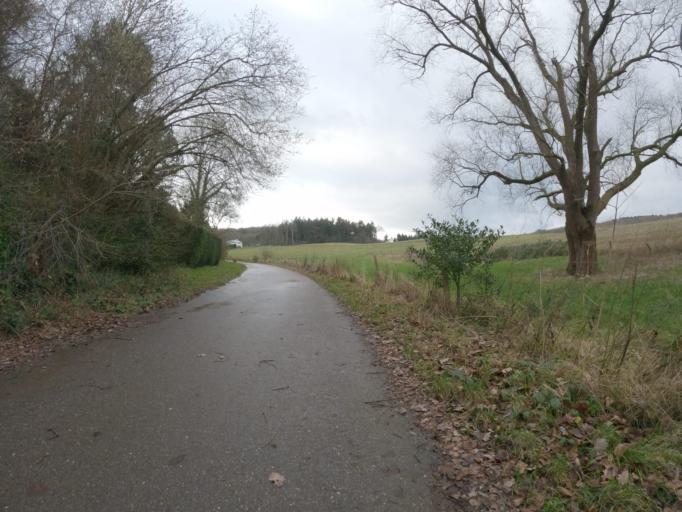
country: DE
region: North Rhine-Westphalia
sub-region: Regierungsbezirk Koln
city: Aachen
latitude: 50.7546
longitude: 6.0525
